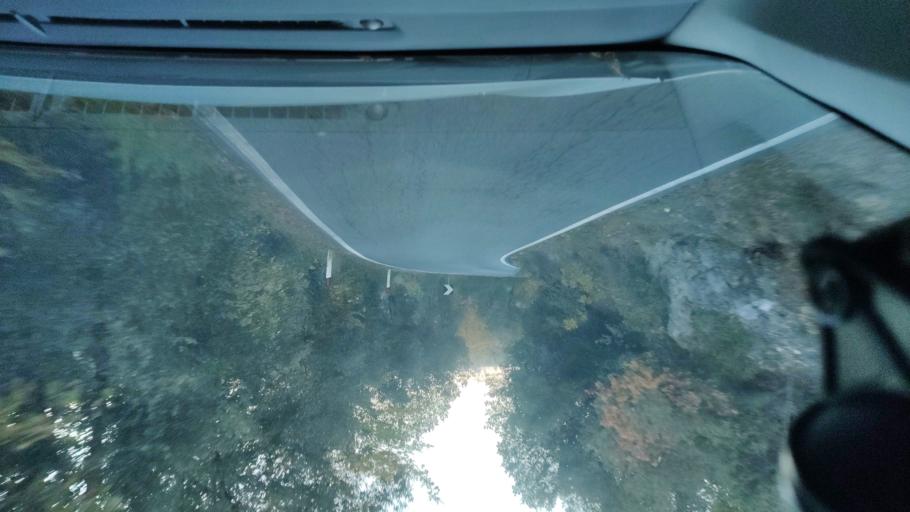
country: IT
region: Umbria
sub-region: Provincia di Terni
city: Amelia
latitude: 42.5883
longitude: 12.4336
